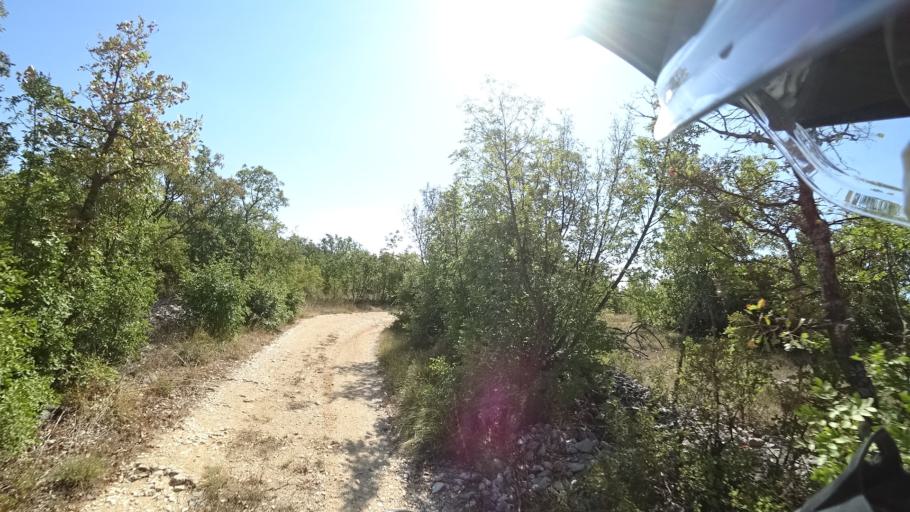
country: HR
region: Sibensko-Kniniska
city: Drnis
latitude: 43.8428
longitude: 16.2850
